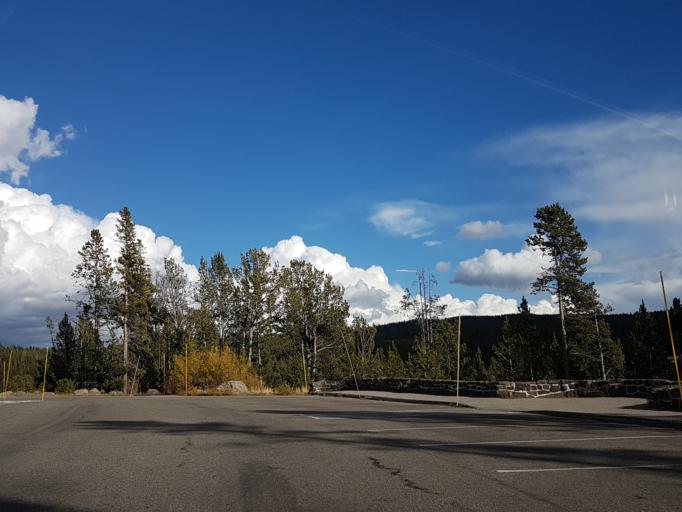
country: US
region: Montana
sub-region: Gallatin County
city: West Yellowstone
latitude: 44.4483
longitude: -110.6922
